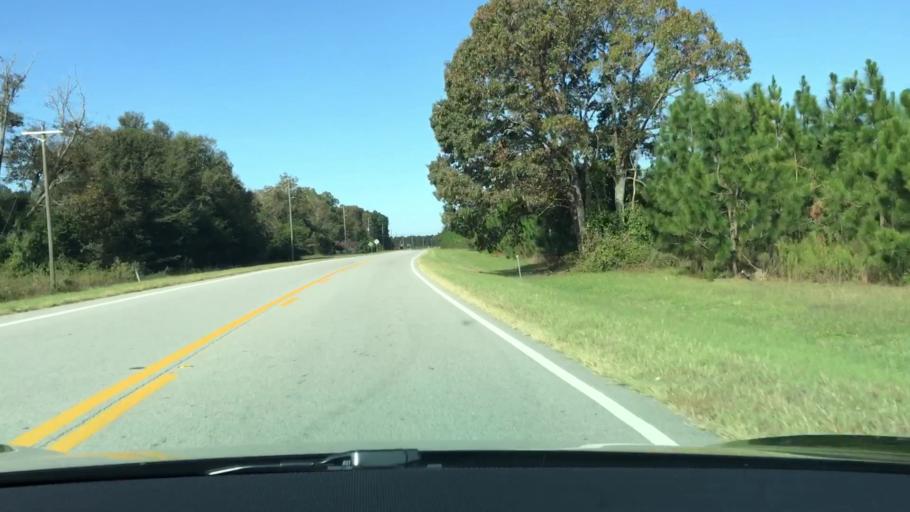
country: US
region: Georgia
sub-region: Glascock County
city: Gibson
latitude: 33.3079
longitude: -82.5321
